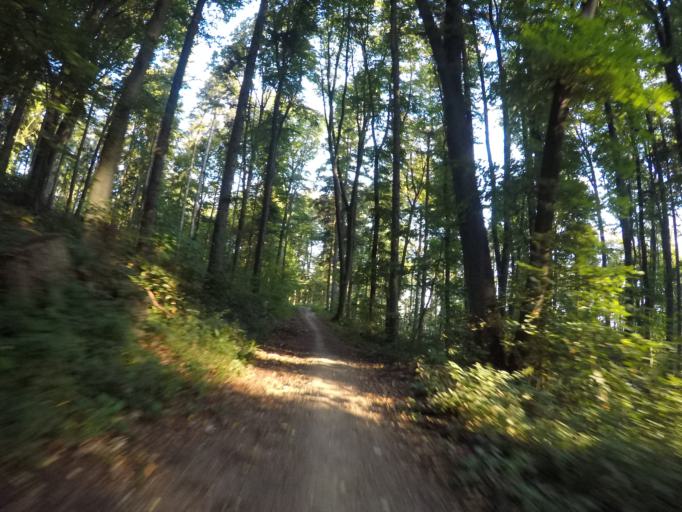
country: SK
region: Kosicky
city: Kosice
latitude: 48.7479
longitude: 21.1899
